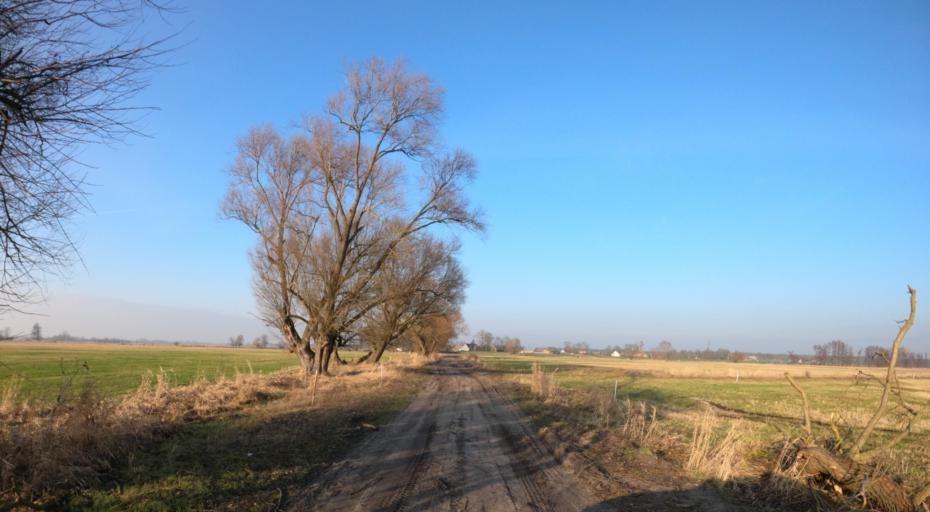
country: DE
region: Brandenburg
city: Zechin
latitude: 52.6580
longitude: 14.5020
